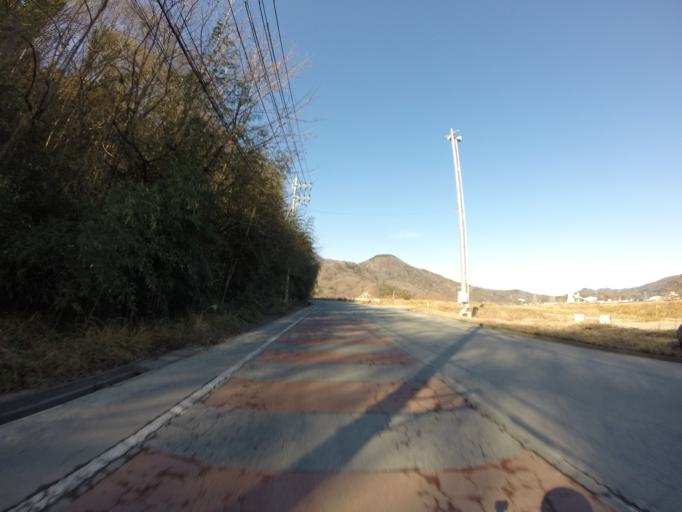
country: JP
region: Yamanashi
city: Ryuo
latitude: 35.4267
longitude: 138.4387
